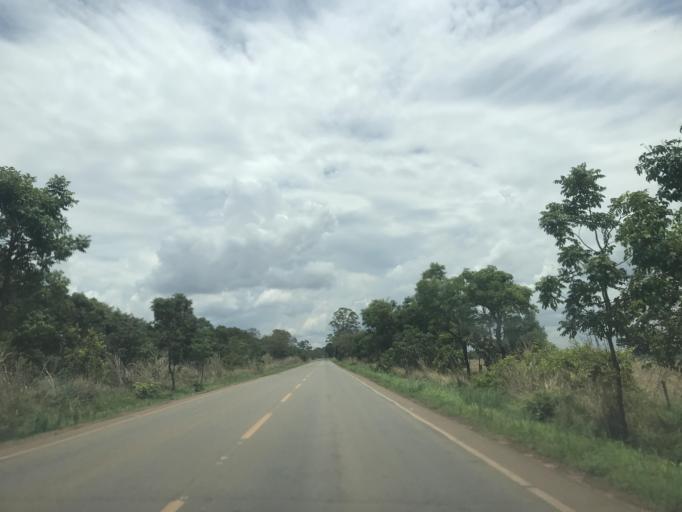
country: BR
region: Goias
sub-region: Vianopolis
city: Vianopolis
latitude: -16.7291
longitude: -48.4412
